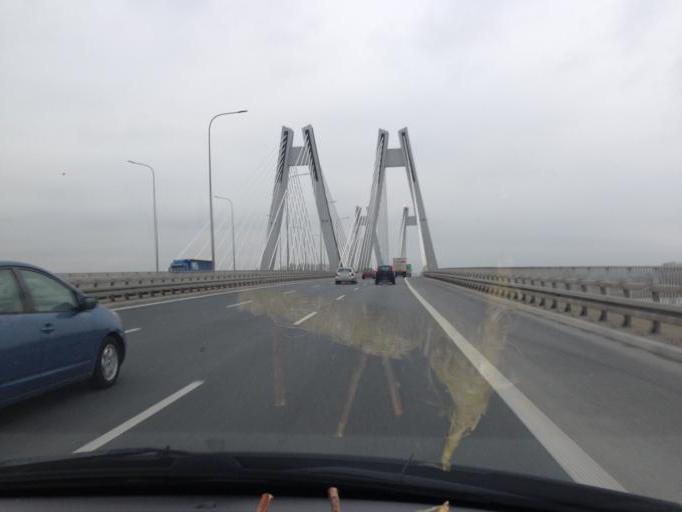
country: PL
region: Lesser Poland Voivodeship
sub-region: Powiat wielicki
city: Kokotow
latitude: 50.0539
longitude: 20.0738
